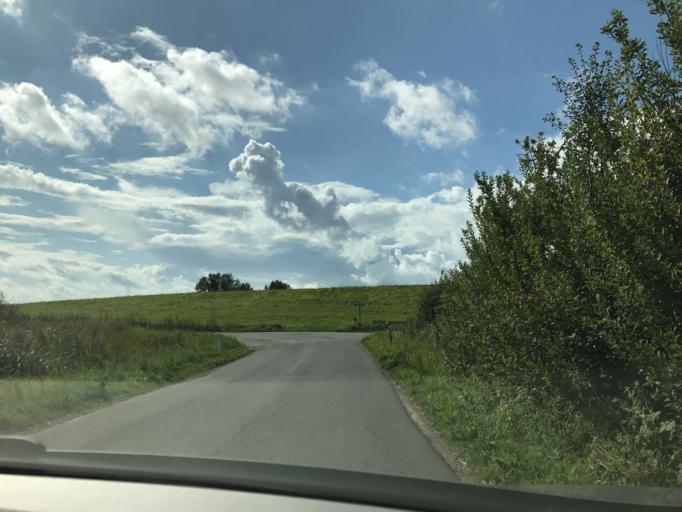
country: DK
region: South Denmark
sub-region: Middelfart Kommune
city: Middelfart
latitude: 55.4569
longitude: 9.7968
